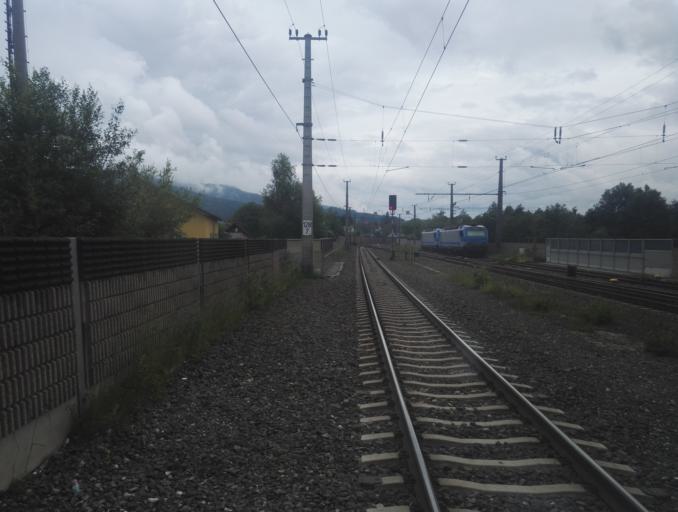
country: AT
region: Styria
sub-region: Politischer Bezirk Bruck-Muerzzuschlag
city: Krieglach
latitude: 47.5463
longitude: 15.5586
